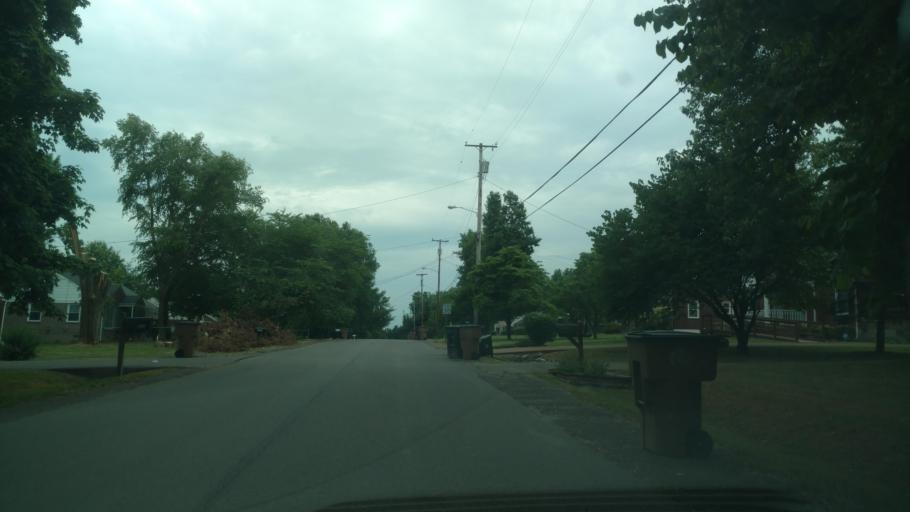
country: US
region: Tennessee
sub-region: Davidson County
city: Nashville
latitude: 36.2051
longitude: -86.7149
